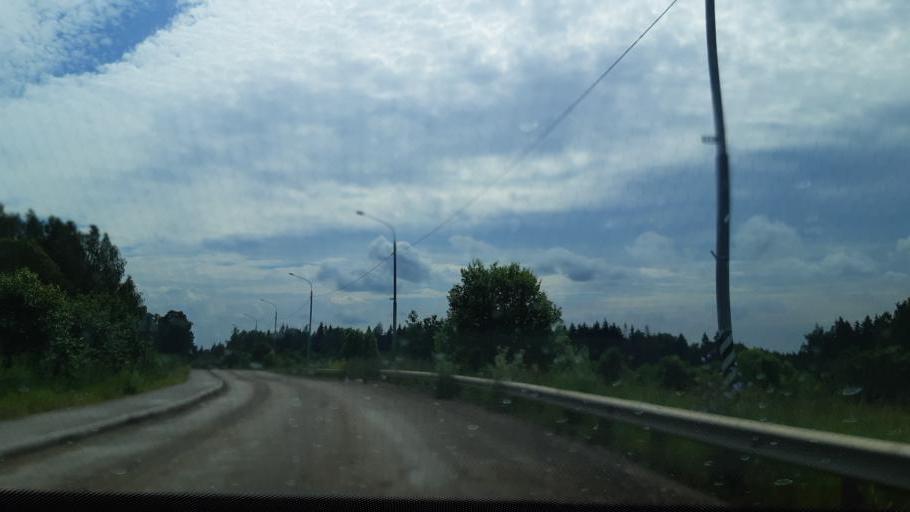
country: RU
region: Moskovskaya
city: Vereya
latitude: 55.2324
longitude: 36.0129
